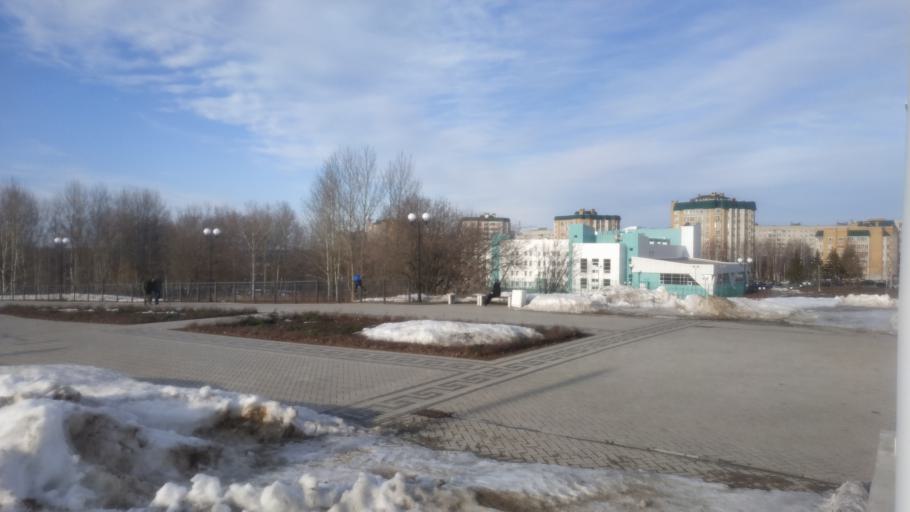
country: RU
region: Chuvashia
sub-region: Cheboksarskiy Rayon
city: Cheboksary
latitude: 56.1462
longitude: 47.2101
